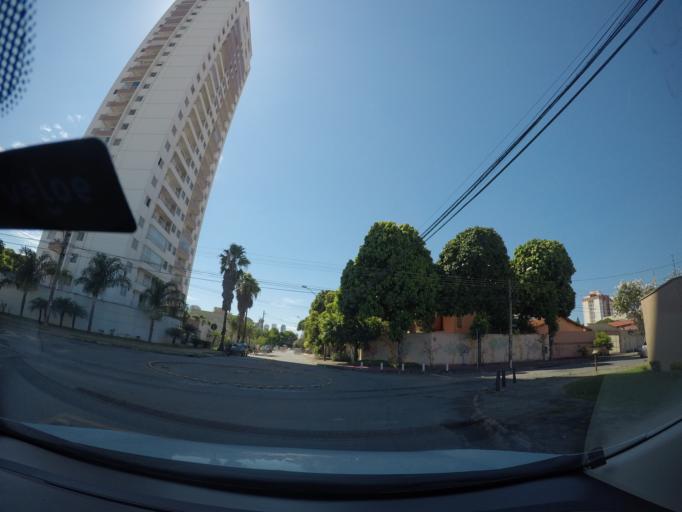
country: BR
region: Goias
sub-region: Goiania
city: Goiania
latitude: -16.6996
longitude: -49.2873
